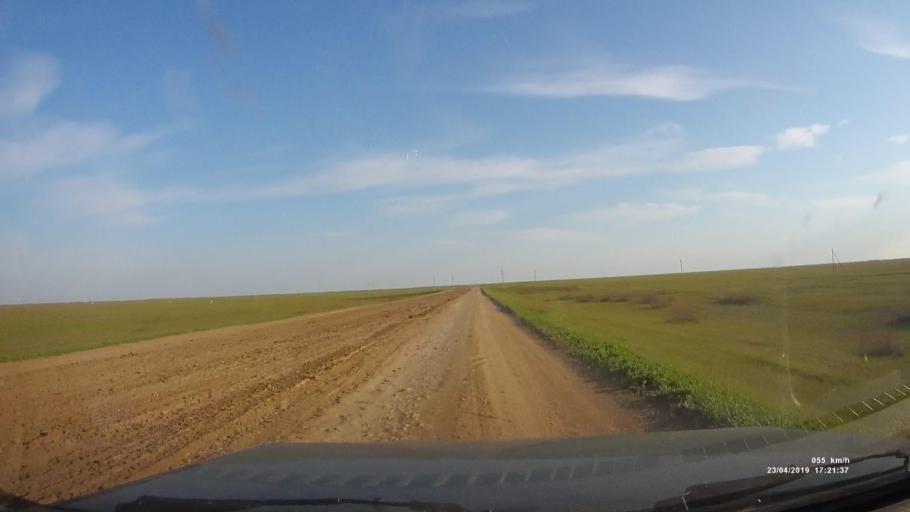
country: RU
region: Kalmykiya
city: Priyutnoye
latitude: 46.1746
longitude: 43.5056
